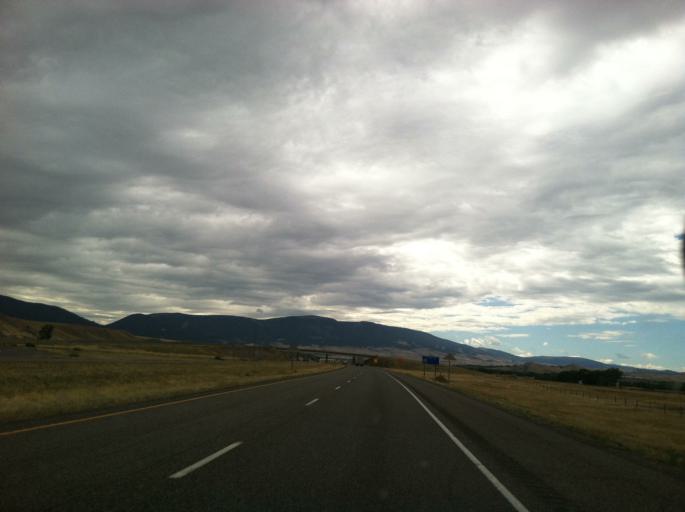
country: US
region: Montana
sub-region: Park County
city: Livingston
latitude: 45.6897
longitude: -110.4976
